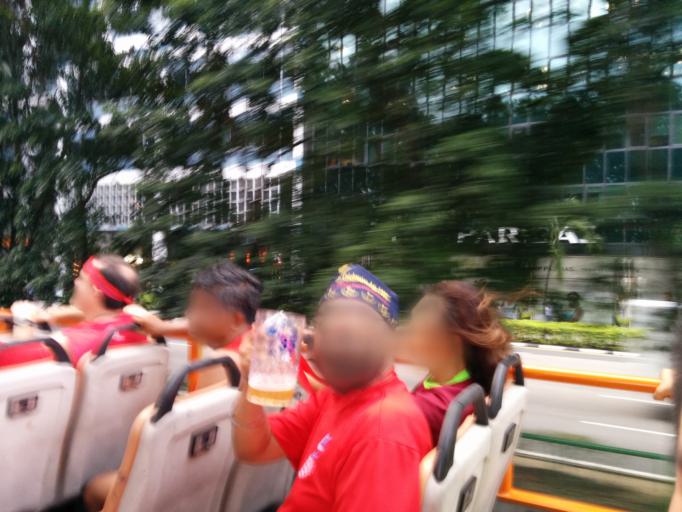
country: SG
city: Singapore
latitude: 1.2846
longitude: 103.8531
